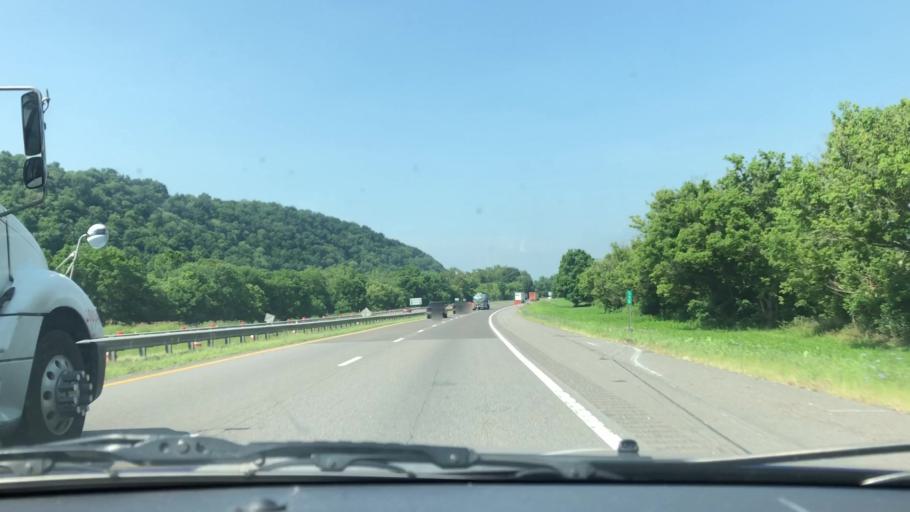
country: US
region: Virginia
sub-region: Smyth County
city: Chilhowie
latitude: 36.7891
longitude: -81.6877
